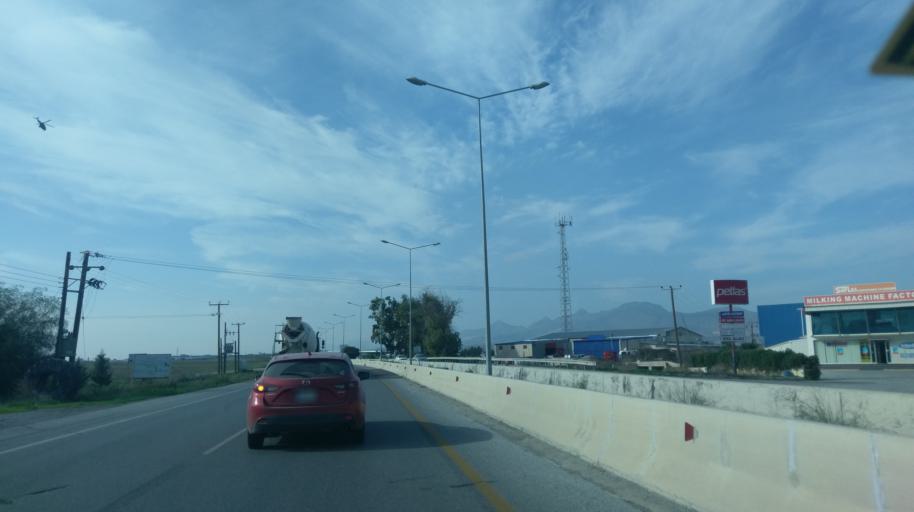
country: CY
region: Lefkosia
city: Geri
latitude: 35.2153
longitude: 33.5118
